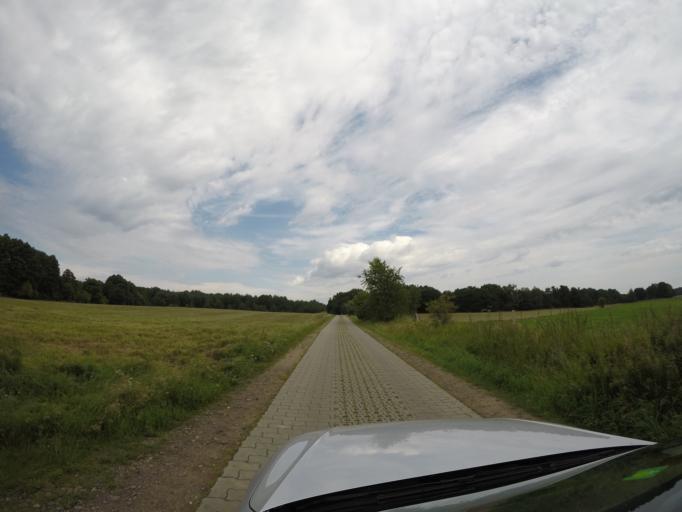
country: DE
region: Mecklenburg-Vorpommern
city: Mollenhagen
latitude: 53.3966
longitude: 12.8970
